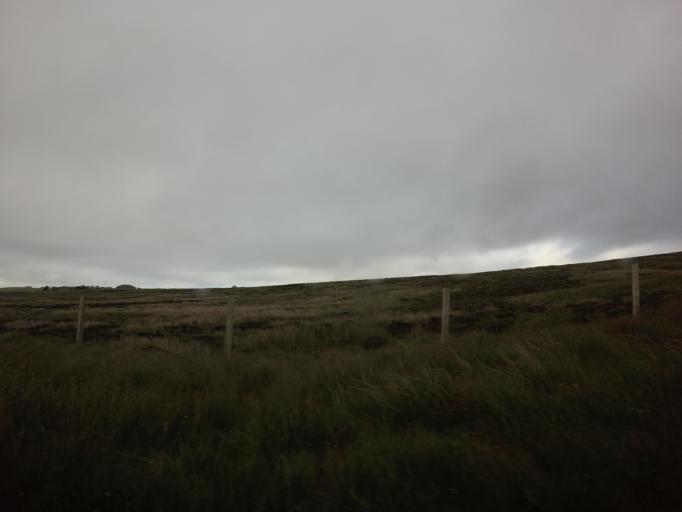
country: GB
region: Scotland
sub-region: Eilean Siar
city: Stornoway
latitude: 58.2067
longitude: -6.2487
